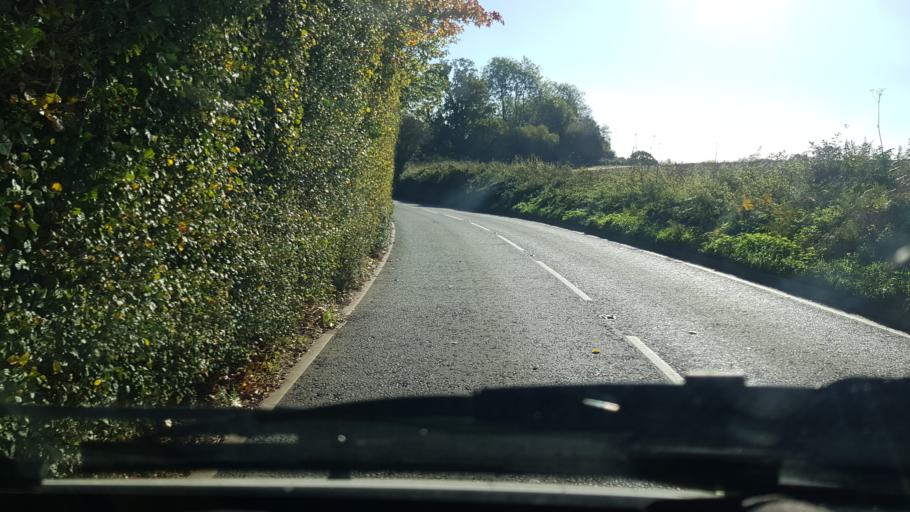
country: GB
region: England
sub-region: Surrey
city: Chilworth
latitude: 51.1790
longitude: -0.5225
